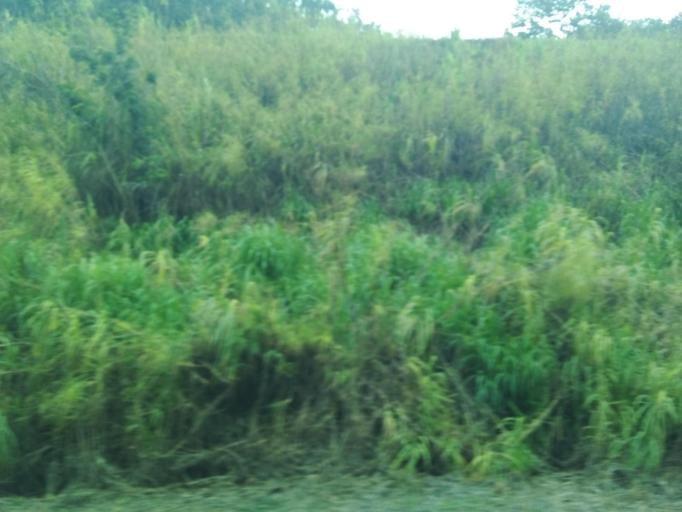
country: BR
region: Minas Gerais
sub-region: Coronel Fabriciano
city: Coronel Fabriciano
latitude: -19.5157
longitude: -42.5750
